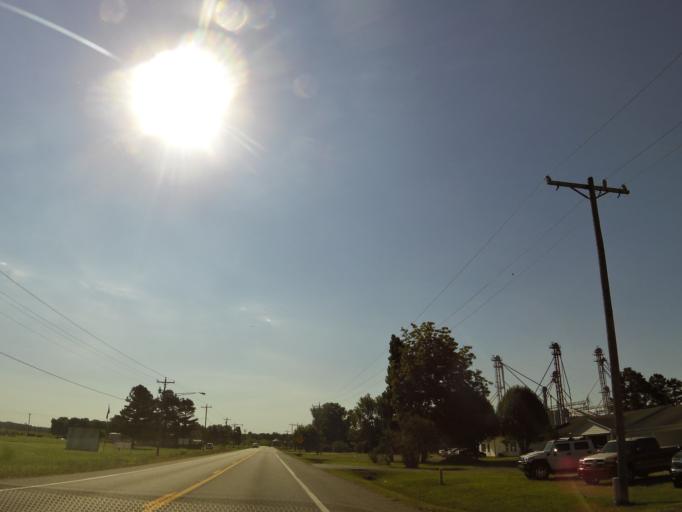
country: US
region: Arkansas
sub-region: Clay County
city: Corning
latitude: 36.4045
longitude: -90.5623
